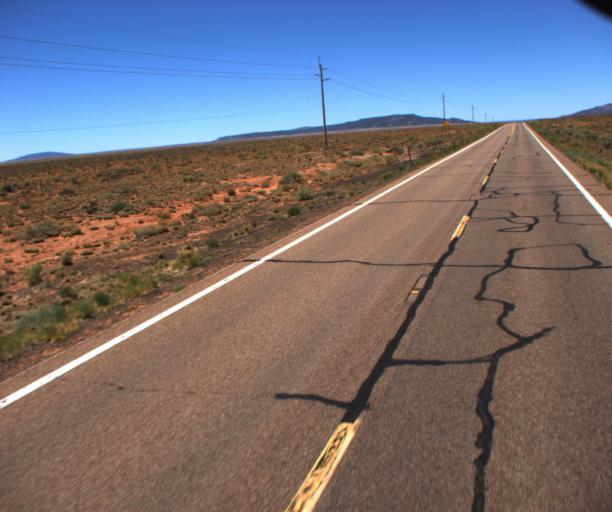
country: US
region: Arizona
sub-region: Coconino County
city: LeChee
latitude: 34.9425
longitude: -110.7765
